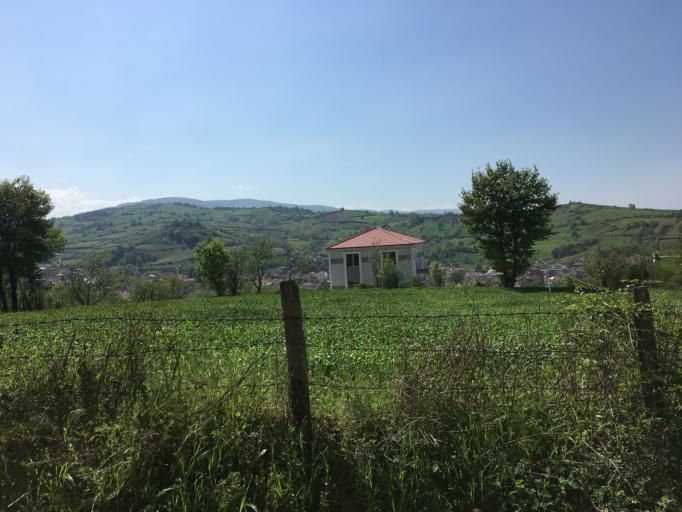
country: TR
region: Samsun
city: Alacam
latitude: 41.6061
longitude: 35.6057
